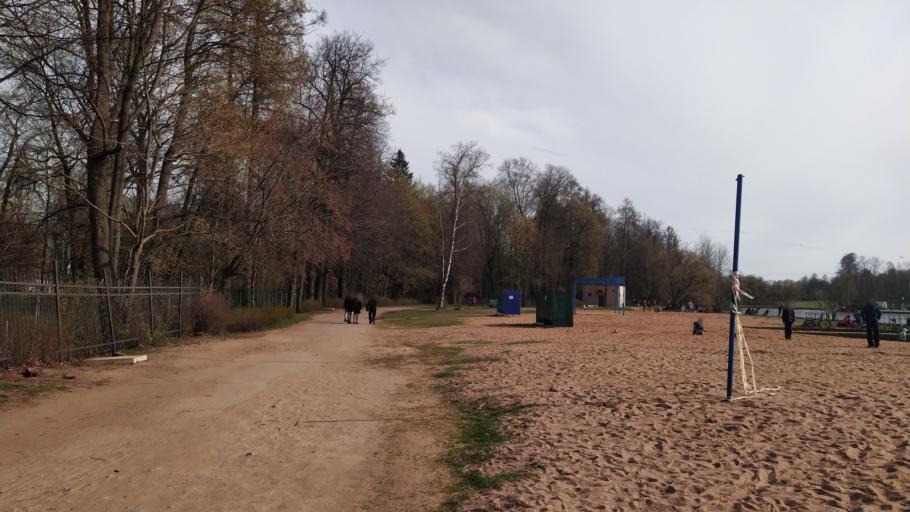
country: RU
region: St.-Petersburg
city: Pushkin
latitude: 59.7144
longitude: 30.4217
